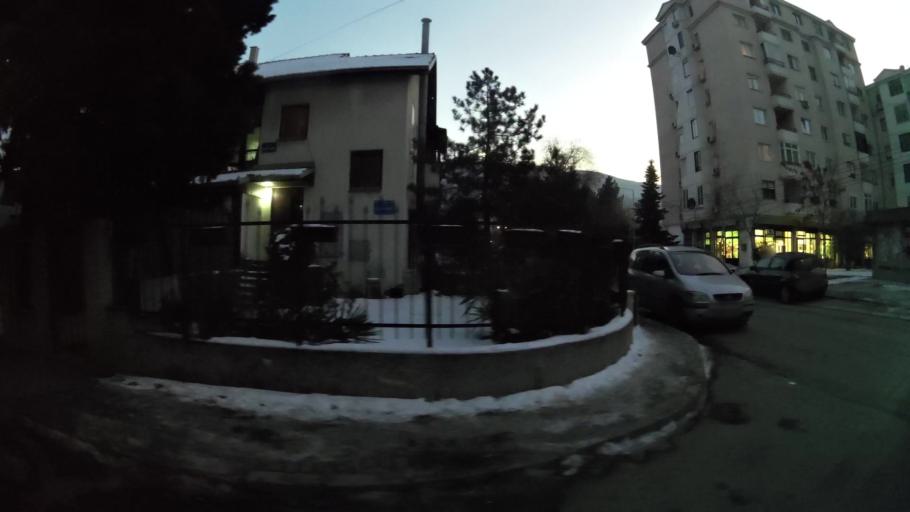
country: MK
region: Karpos
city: Skopje
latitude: 41.9980
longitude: 21.4062
